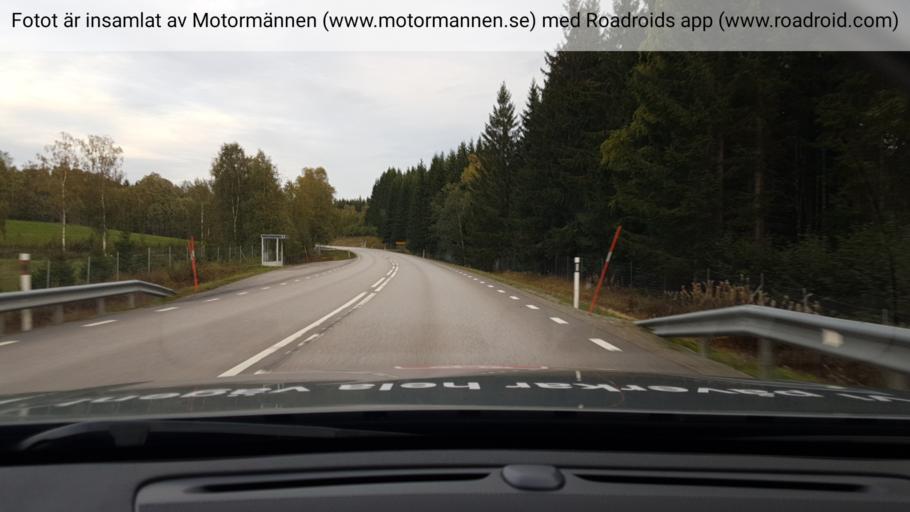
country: SE
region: Vaestra Goetaland
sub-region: Bengtsfors Kommun
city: Billingsfors
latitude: 59.0218
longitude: 12.3692
